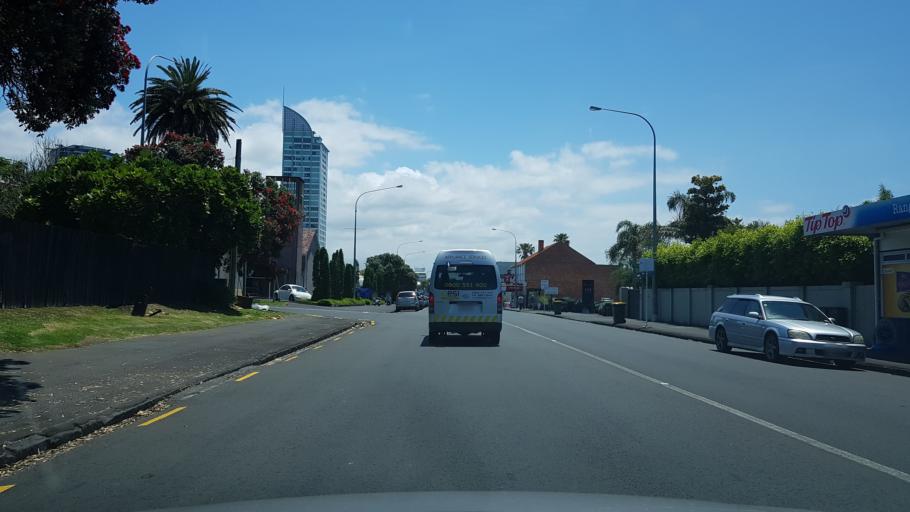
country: NZ
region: Auckland
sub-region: Auckland
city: North Shore
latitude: -36.7926
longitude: 174.7750
